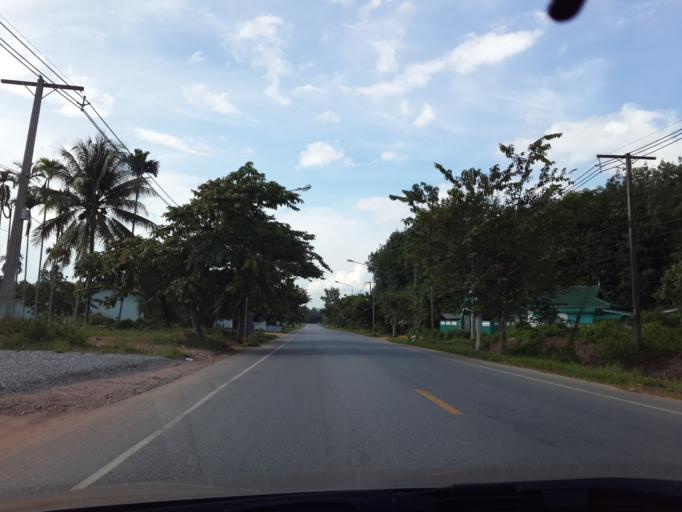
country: TH
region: Yala
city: Krong Pi Nang
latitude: 6.4639
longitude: 101.3290
